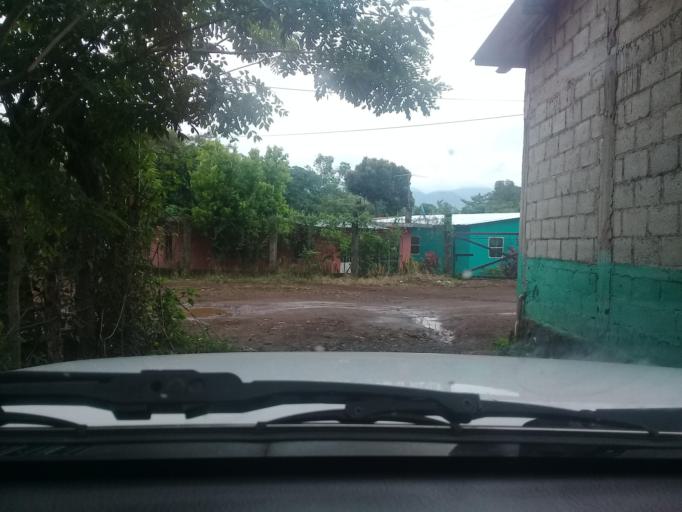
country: MX
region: Veracruz
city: Comoapan
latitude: 18.4053
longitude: -95.1781
